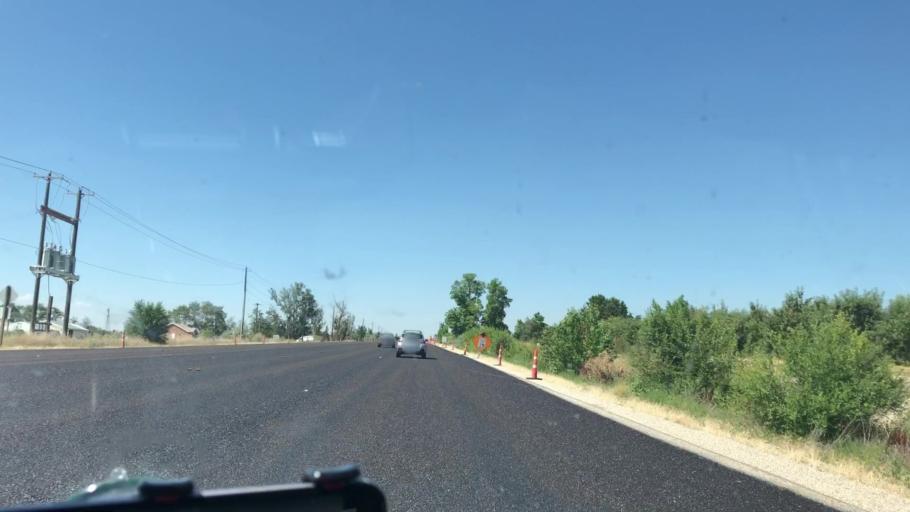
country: US
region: Idaho
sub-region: Owyhee County
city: Marsing
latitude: 43.5895
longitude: -116.7922
